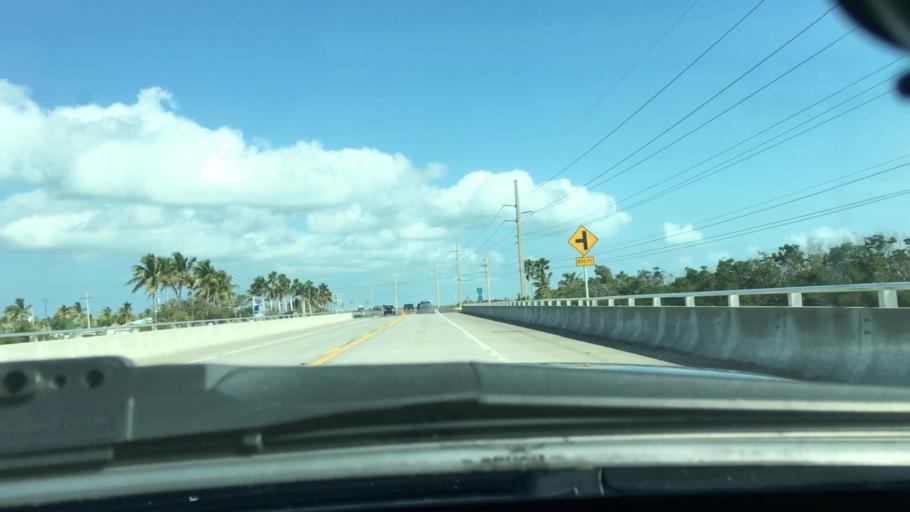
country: US
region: Florida
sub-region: Monroe County
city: Big Pine Key
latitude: 24.6708
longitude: -81.2490
